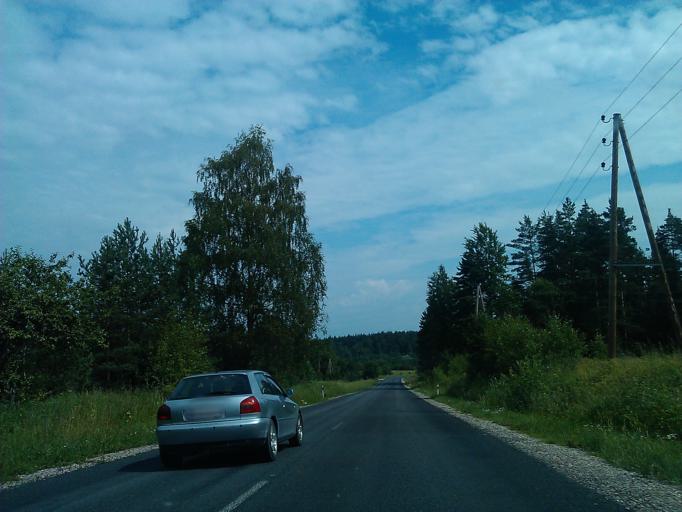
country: LV
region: Priekuli
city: Priekuli
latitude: 57.3585
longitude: 25.3648
